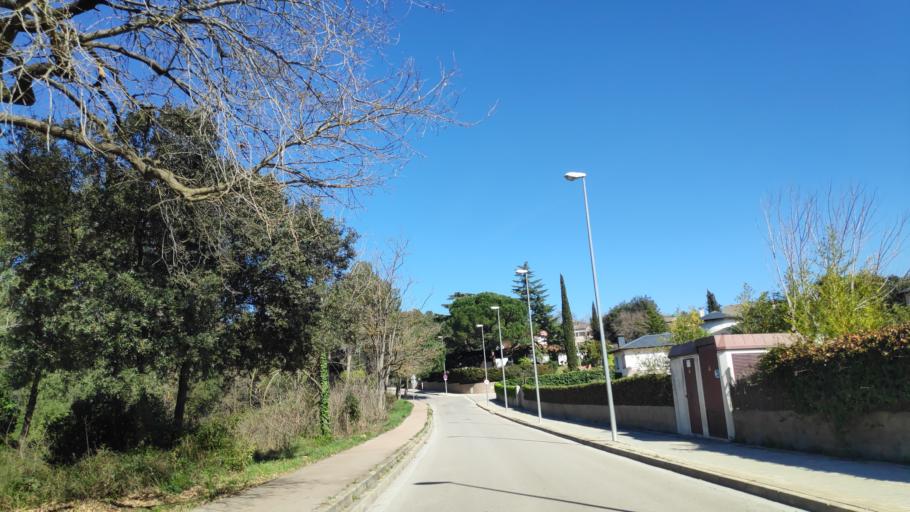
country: ES
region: Catalonia
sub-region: Provincia de Barcelona
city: Sant Quirze del Valles
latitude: 41.5596
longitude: 2.0693
